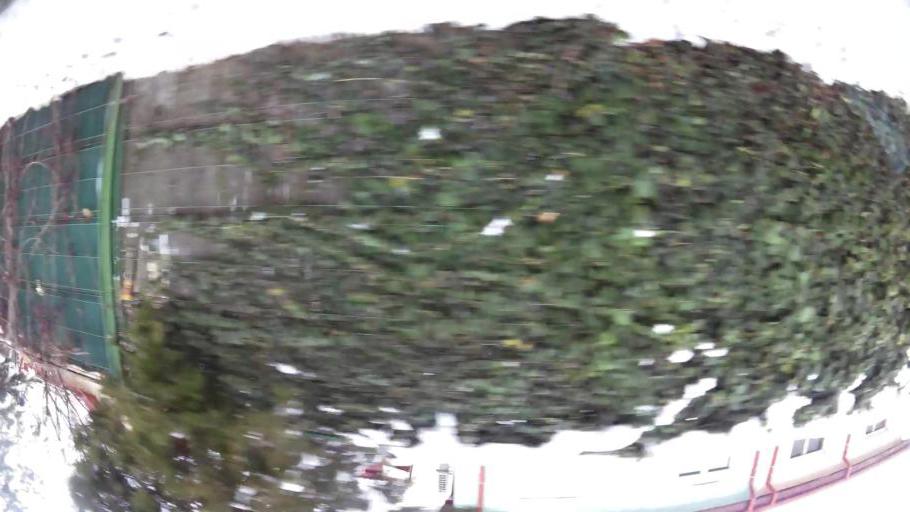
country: RO
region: Ilfov
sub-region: Comuna Tunari
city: Tunari
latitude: 44.5117
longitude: 26.1142
